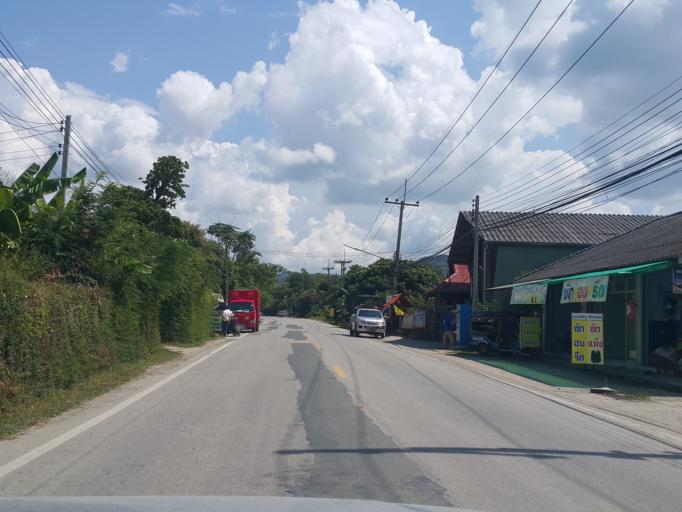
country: TH
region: Chiang Mai
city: San Kamphaeng
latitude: 18.7243
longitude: 99.1677
